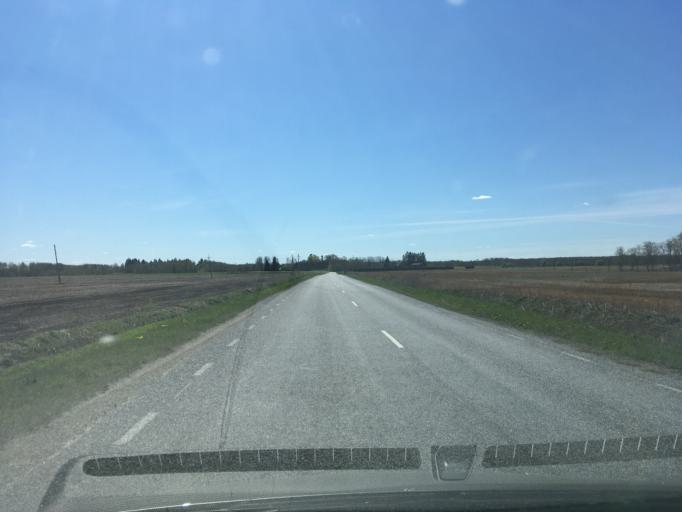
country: EE
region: Harju
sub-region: Raasiku vald
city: Arukula
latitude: 59.4163
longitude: 25.0782
